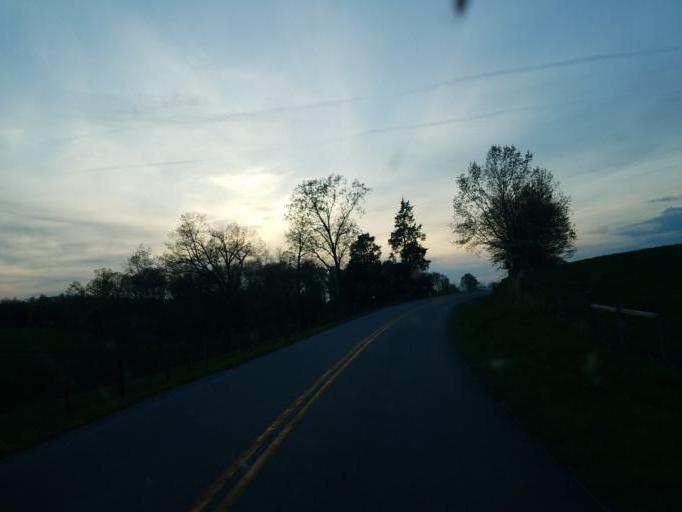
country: US
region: Kentucky
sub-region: Hart County
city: Munfordville
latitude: 37.2443
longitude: -85.7567
